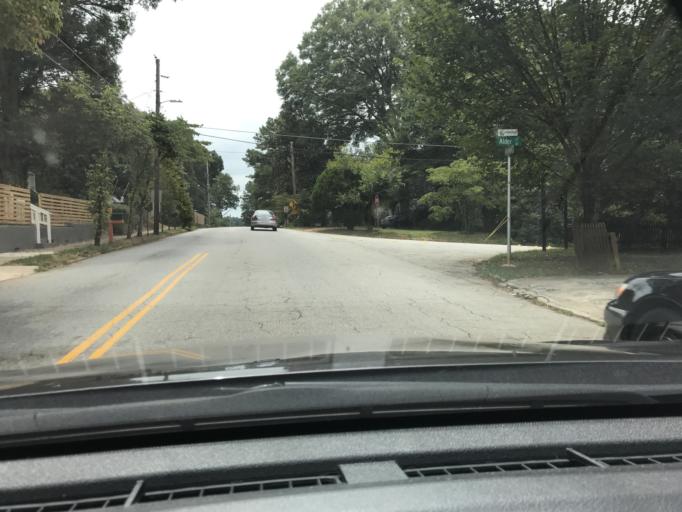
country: US
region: Georgia
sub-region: DeKalb County
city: Druid Hills
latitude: 33.7498
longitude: -84.3332
